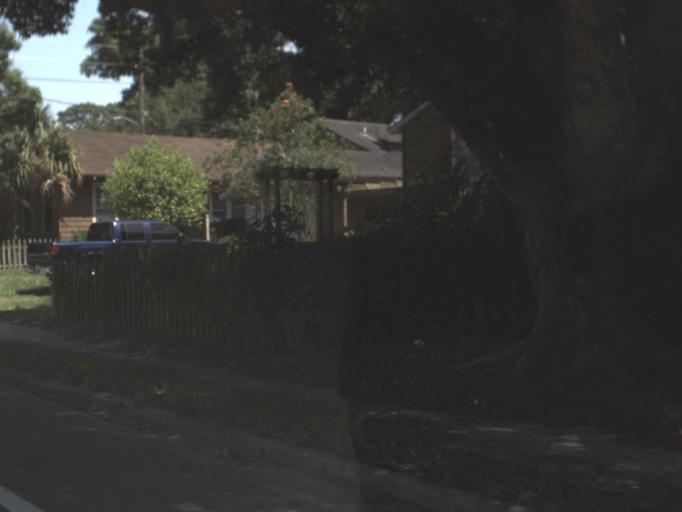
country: US
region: Florida
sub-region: Duval County
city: Jacksonville
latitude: 30.3090
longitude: -81.7227
